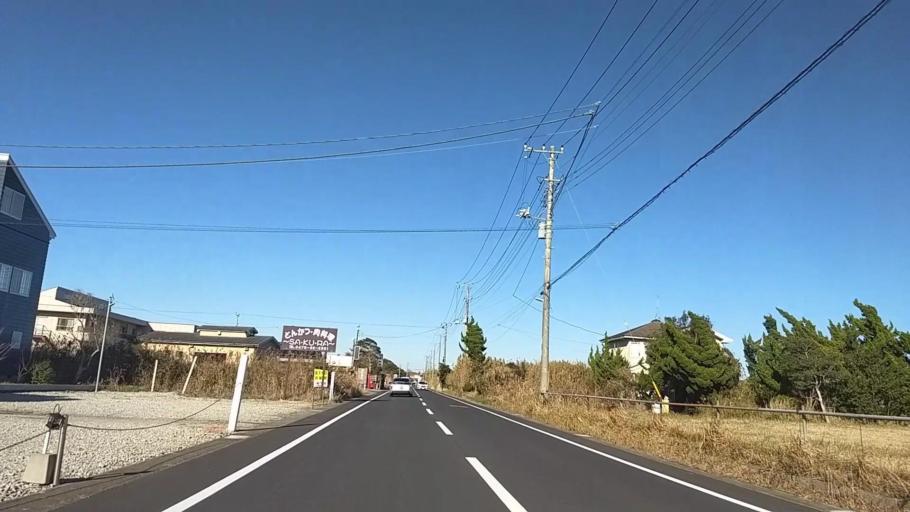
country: JP
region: Chiba
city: Mobara
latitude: 35.4092
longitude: 140.3883
